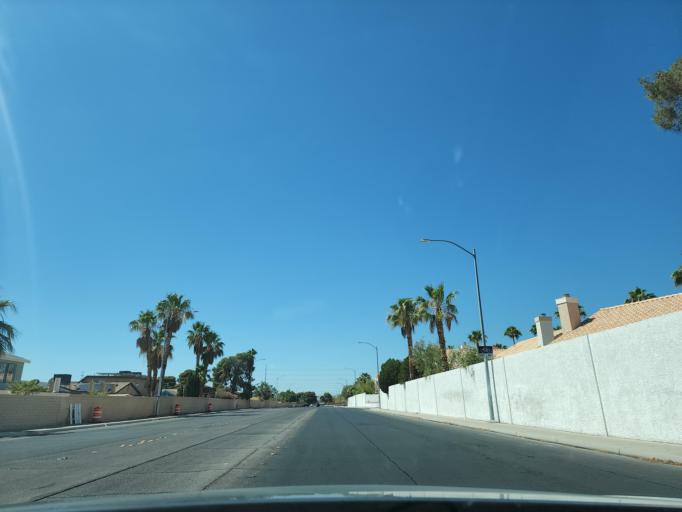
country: US
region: Nevada
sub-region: Clark County
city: Spring Valley
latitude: 36.1182
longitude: -115.2521
